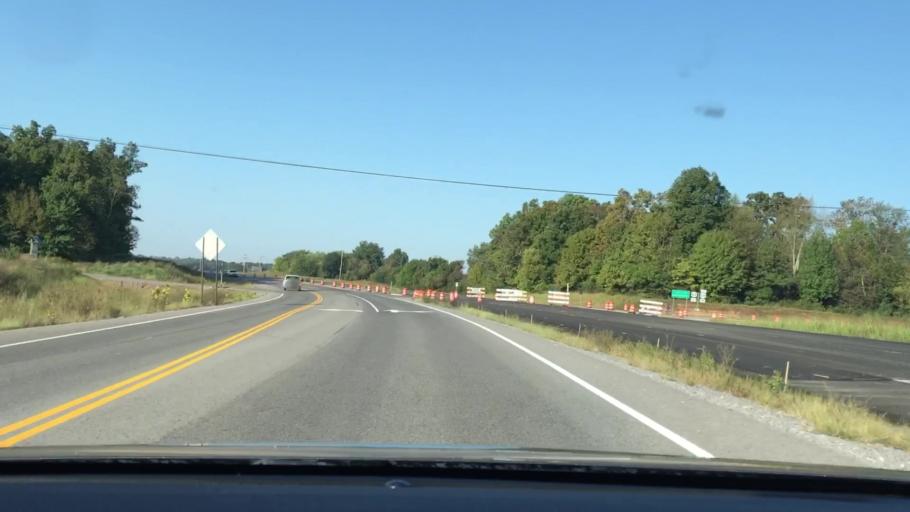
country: US
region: Kentucky
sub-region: Trigg County
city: Cadiz
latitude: 36.8391
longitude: -87.8591
